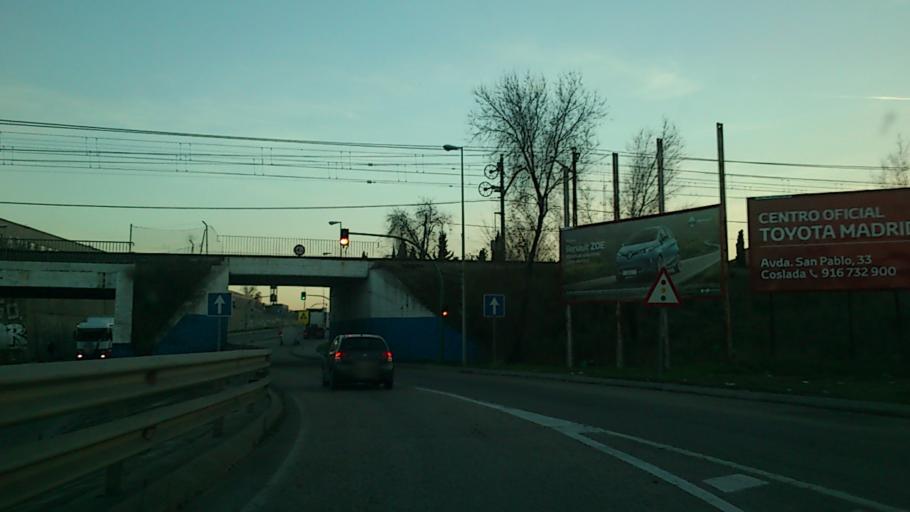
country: ES
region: Madrid
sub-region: Provincia de Madrid
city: San Fernando de Henares
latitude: 40.4410
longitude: -3.5422
